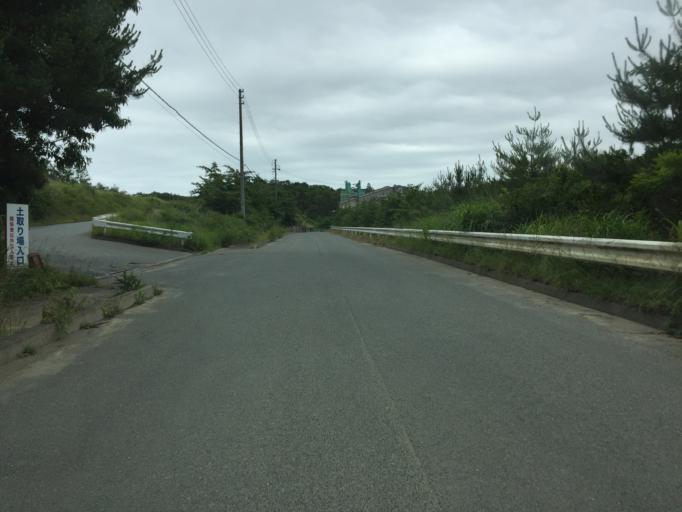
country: JP
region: Miyagi
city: Marumori
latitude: 37.7512
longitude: 140.9659
